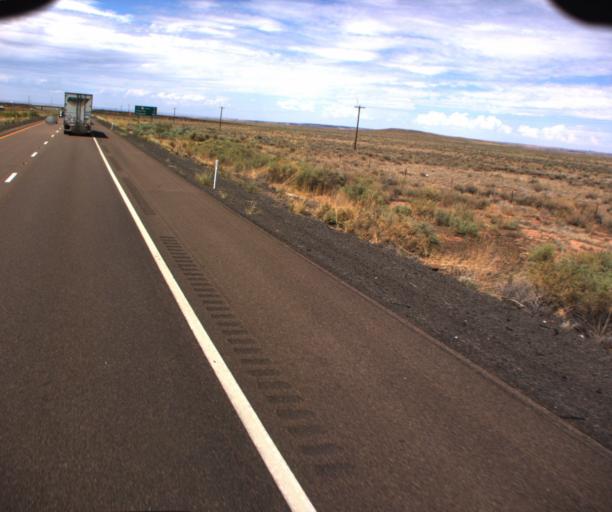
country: US
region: Arizona
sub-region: Navajo County
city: Holbrook
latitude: 35.0523
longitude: -109.7957
